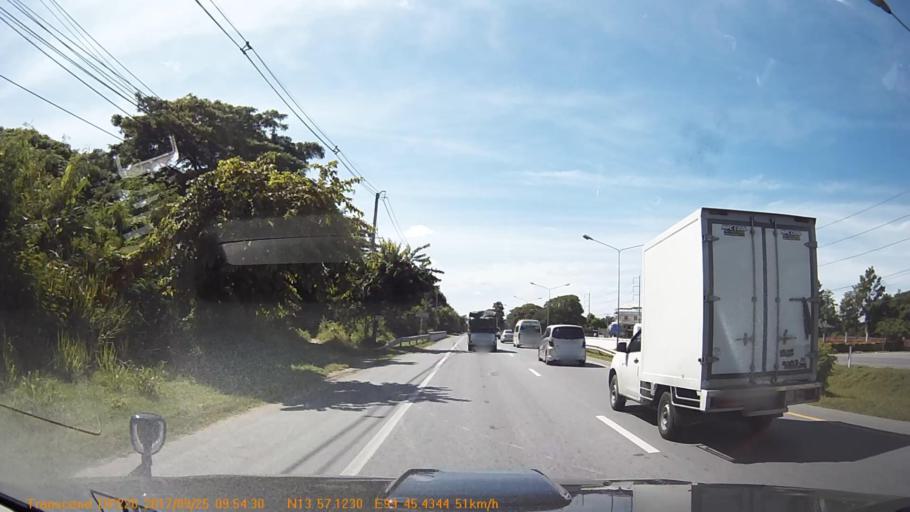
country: TH
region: Kanchanaburi
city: Tha Maka
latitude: 13.9518
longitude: 99.7573
